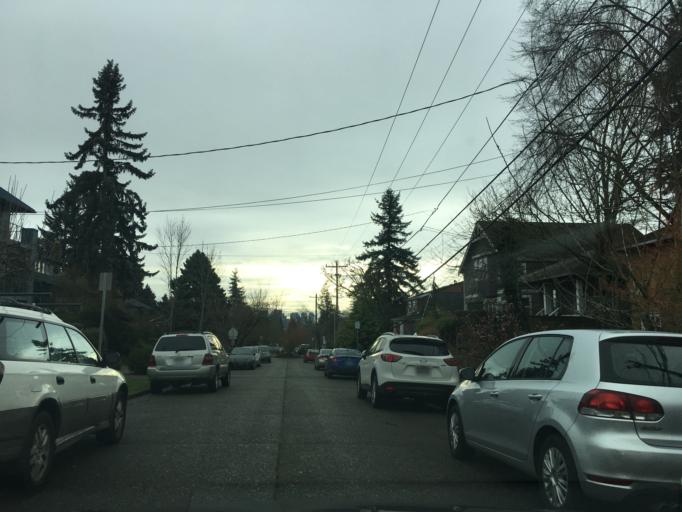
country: US
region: Washington
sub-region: King County
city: Seattle
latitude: 47.6589
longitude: -122.3407
